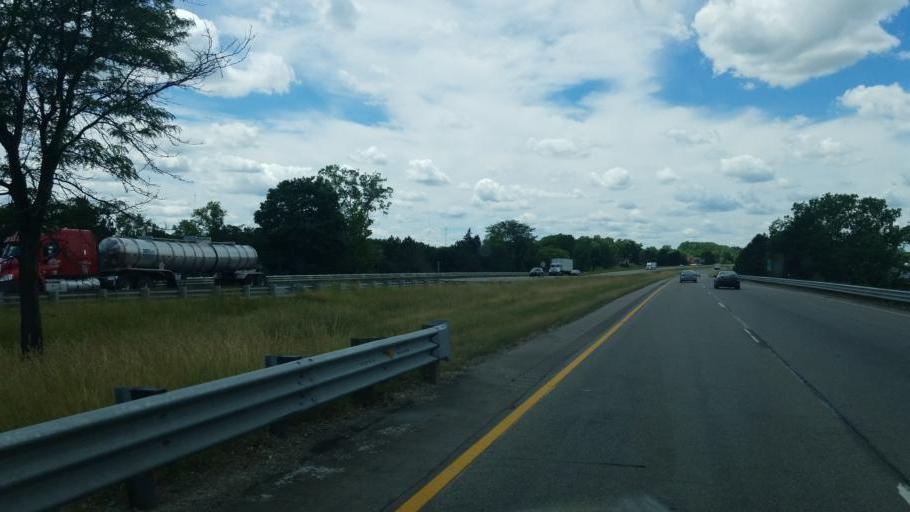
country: US
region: Michigan
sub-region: Ingham County
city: Holt
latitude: 42.6604
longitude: -84.5381
